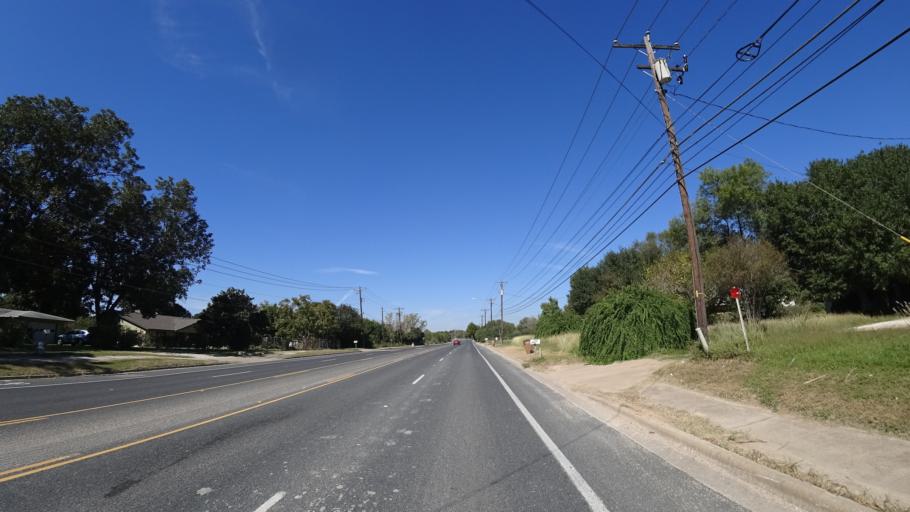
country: US
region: Texas
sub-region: Travis County
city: Austin
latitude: 30.1877
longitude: -97.6937
